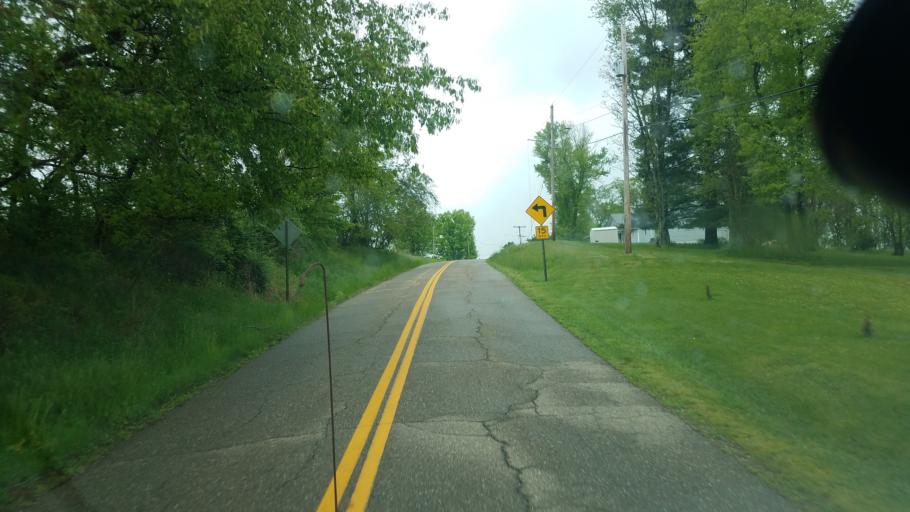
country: US
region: Ohio
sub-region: Jefferson County
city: Tiltonsville
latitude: 40.2103
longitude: -80.6886
